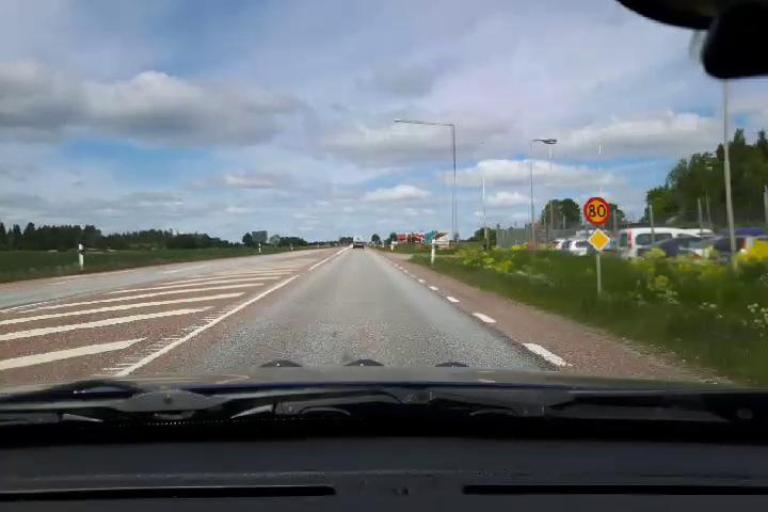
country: SE
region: Uppsala
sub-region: Uppsala Kommun
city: Gamla Uppsala
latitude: 59.9344
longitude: 17.5960
